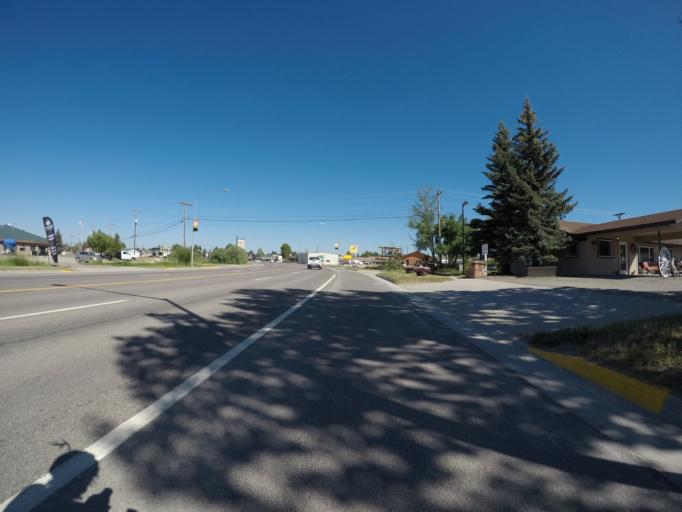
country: US
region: Wyoming
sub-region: Sublette County
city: Pinedale
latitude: 42.8652
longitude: -109.8545
